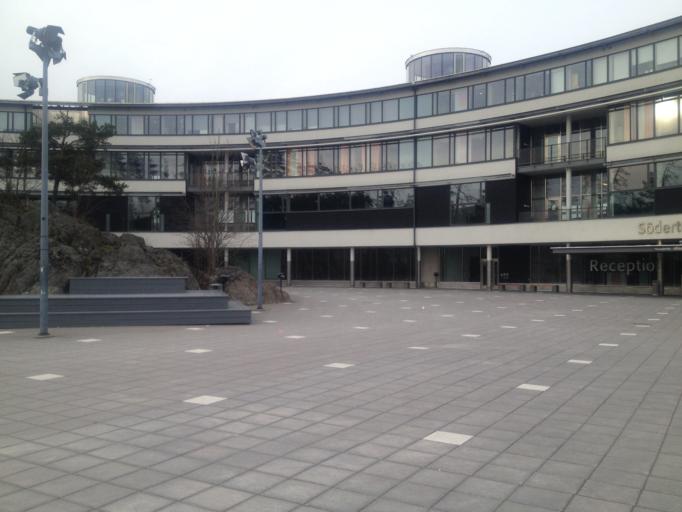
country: SE
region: Stockholm
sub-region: Huddinge Kommun
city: Huddinge
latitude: 59.2191
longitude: 17.9430
